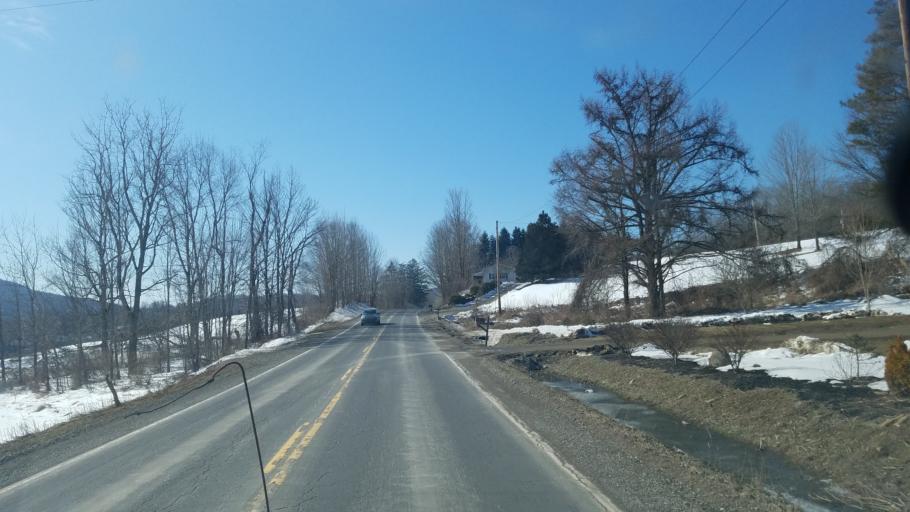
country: US
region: New York
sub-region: Steuben County
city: Hornell
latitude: 42.3594
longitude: -77.7013
